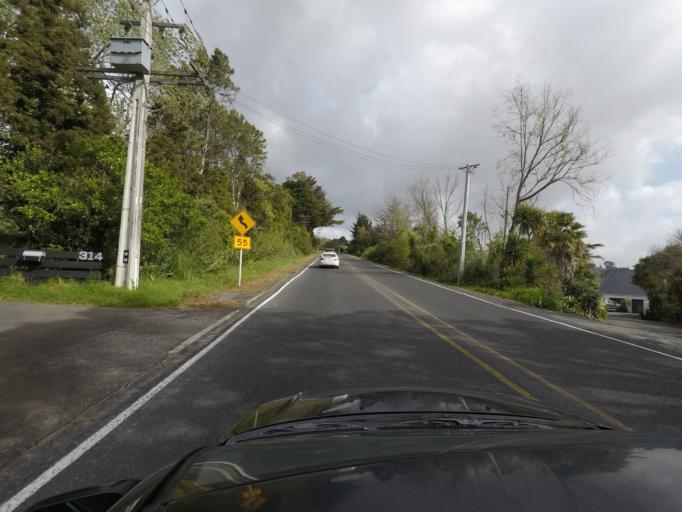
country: NZ
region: Auckland
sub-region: Auckland
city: Pakuranga
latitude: -36.9280
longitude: 174.9356
